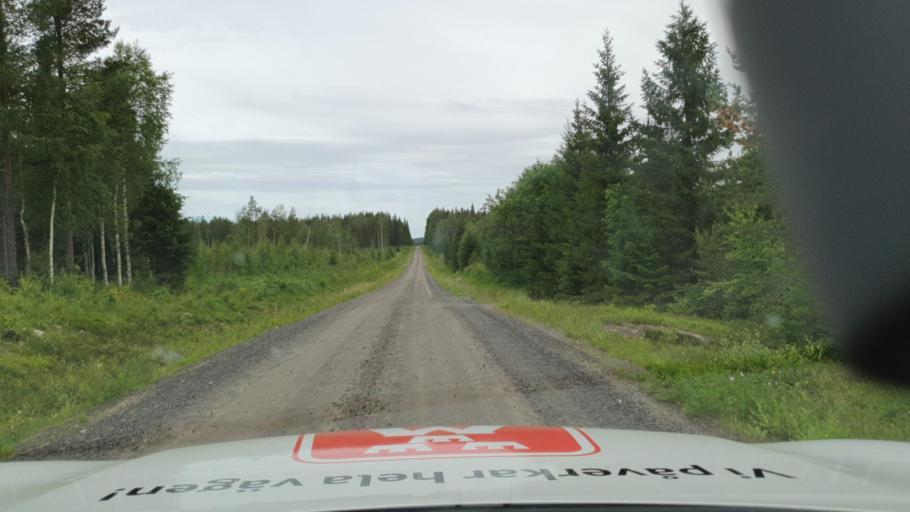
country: SE
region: Vaesterbotten
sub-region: Skelleftea Kommun
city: Burtraesk
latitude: 64.3729
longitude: 20.6158
